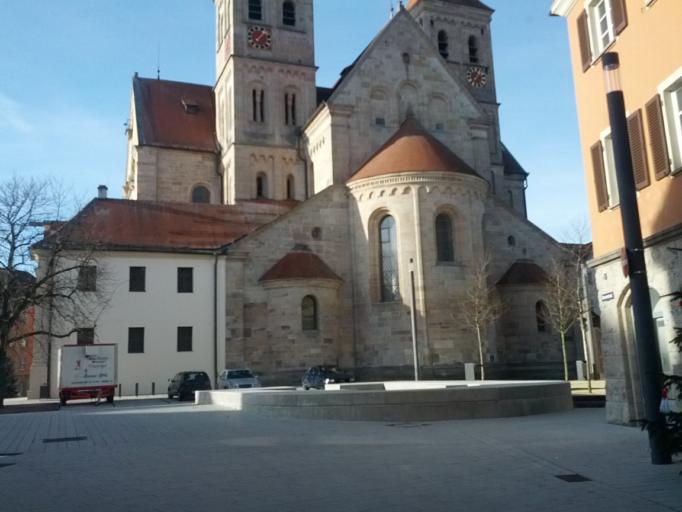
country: DE
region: Baden-Wuerttemberg
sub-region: Regierungsbezirk Stuttgart
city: Ellwangen
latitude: 48.9618
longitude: 10.1331
